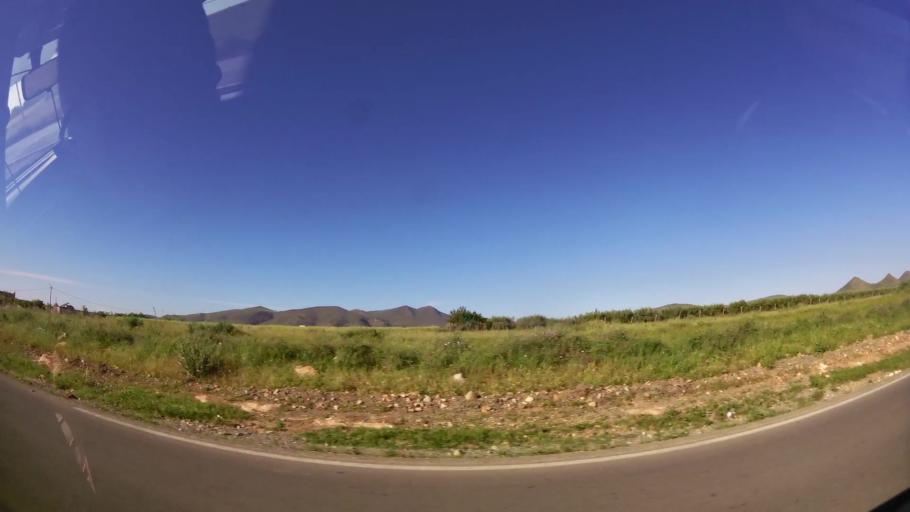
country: MA
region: Oriental
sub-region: Berkane-Taourirt
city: Ahfir
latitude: 34.9675
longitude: -2.1183
